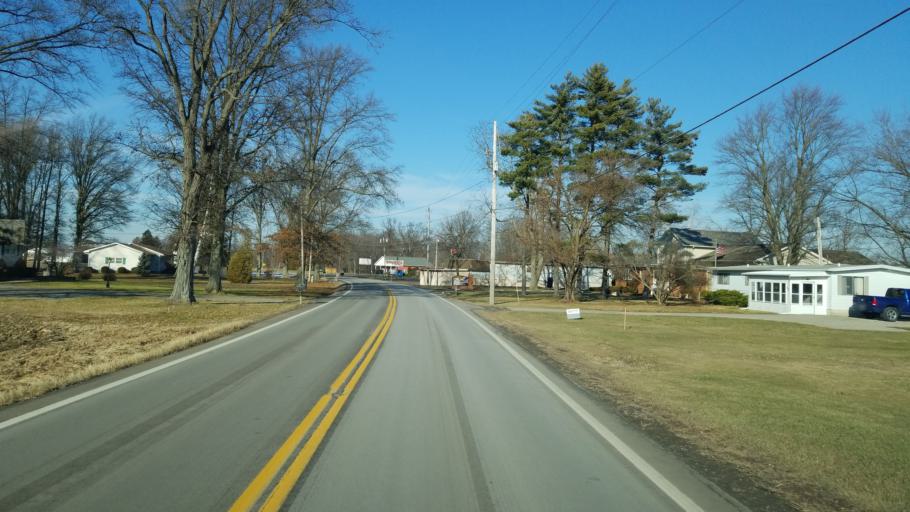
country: US
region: Ohio
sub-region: Huron County
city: Norwalk
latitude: 41.2163
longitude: -82.6385
